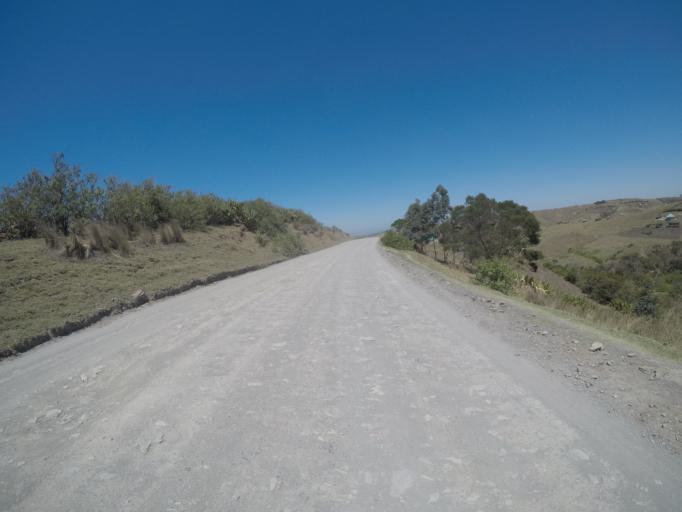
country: ZA
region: Eastern Cape
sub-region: OR Tambo District Municipality
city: Libode
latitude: -31.9904
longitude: 29.0538
